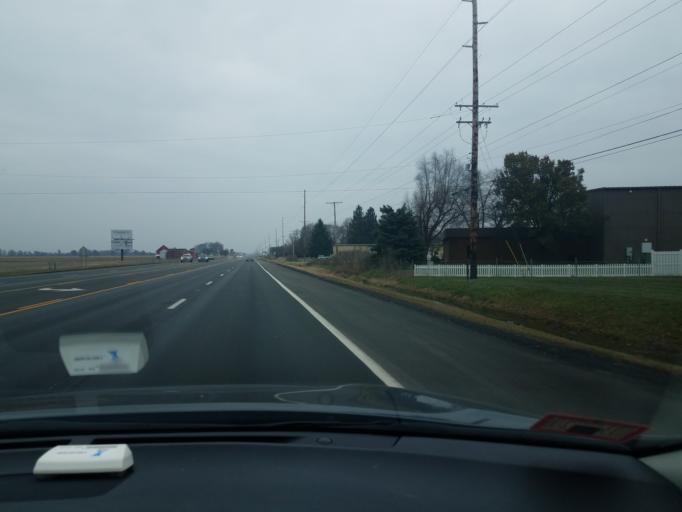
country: US
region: Ohio
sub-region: Erie County
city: Milan
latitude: 41.3764
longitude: -82.6434
